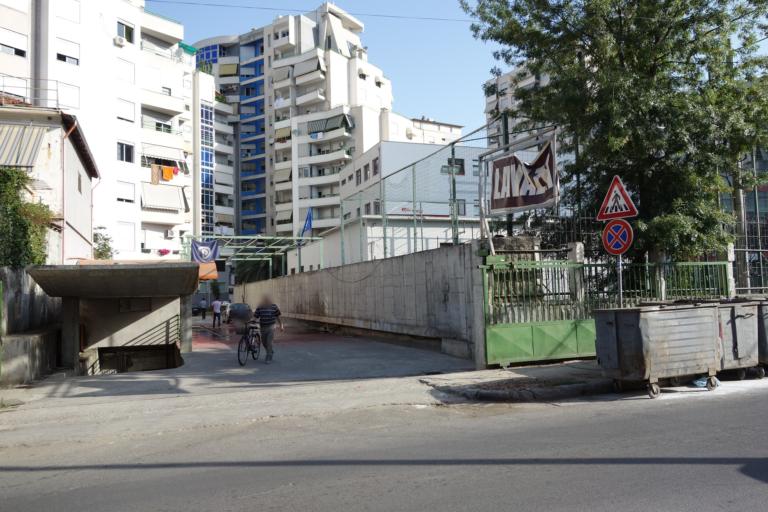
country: AL
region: Tirane
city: Tirana
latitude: 41.3338
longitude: 19.8245
